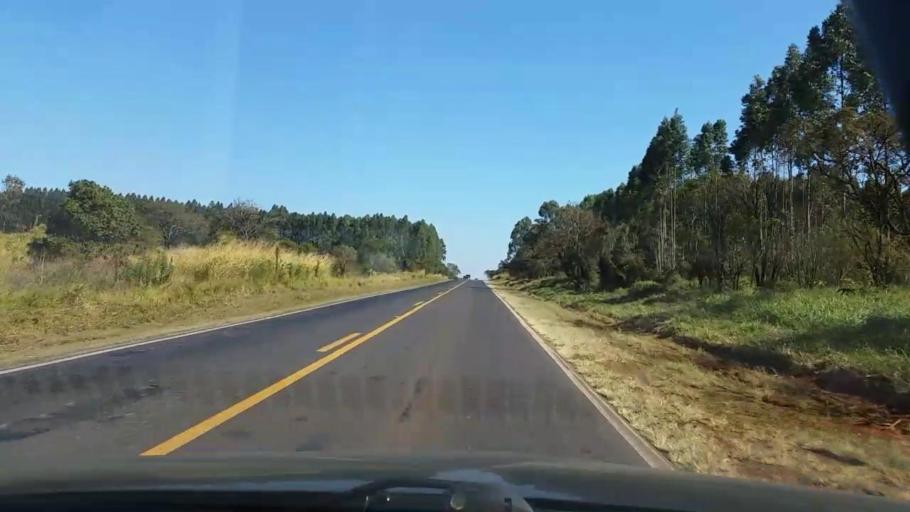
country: BR
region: Sao Paulo
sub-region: Avare
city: Avare
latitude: -22.9196
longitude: -48.7826
